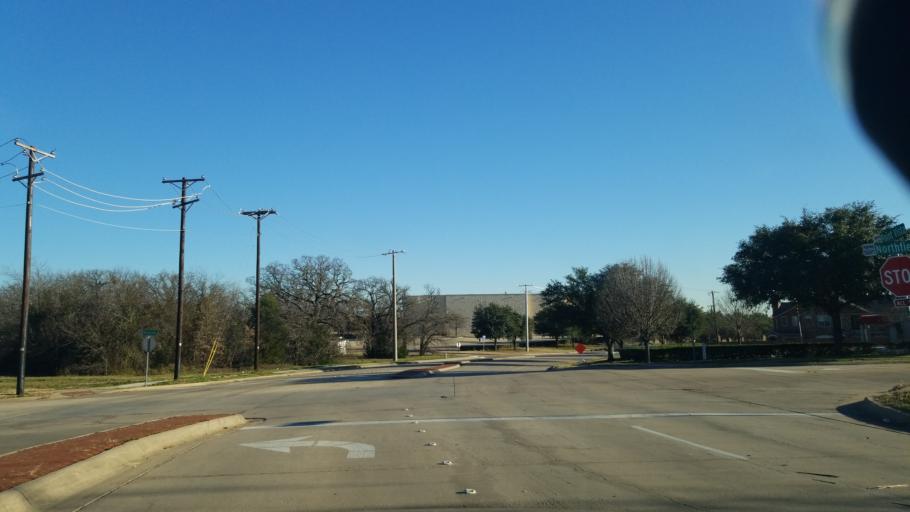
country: US
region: Texas
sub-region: Denton County
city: Hickory Creek
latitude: 33.1266
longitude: -97.0394
